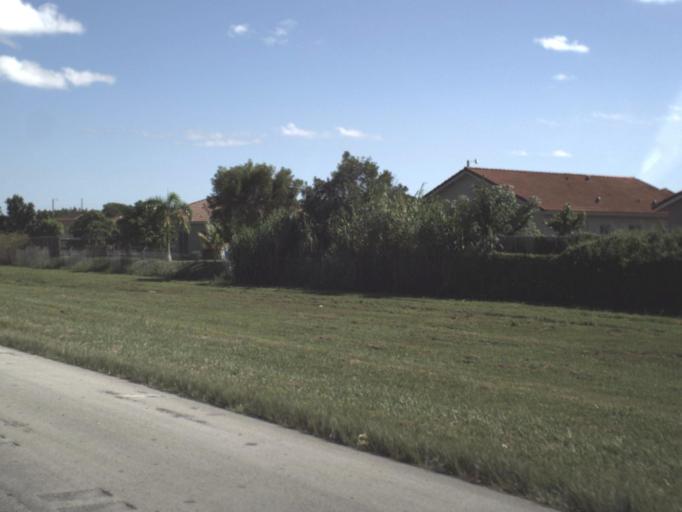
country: US
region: Florida
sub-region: Miami-Dade County
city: Homestead
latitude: 25.4650
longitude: -80.4584
